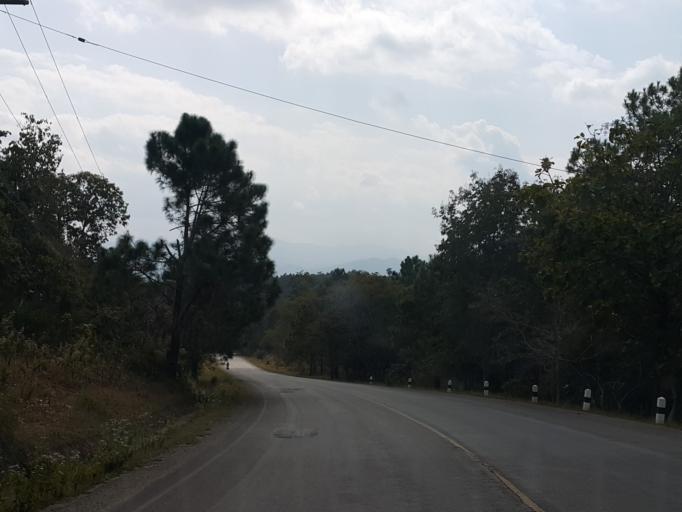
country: TH
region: Chiang Mai
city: Om Koi
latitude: 17.8580
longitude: 98.3726
